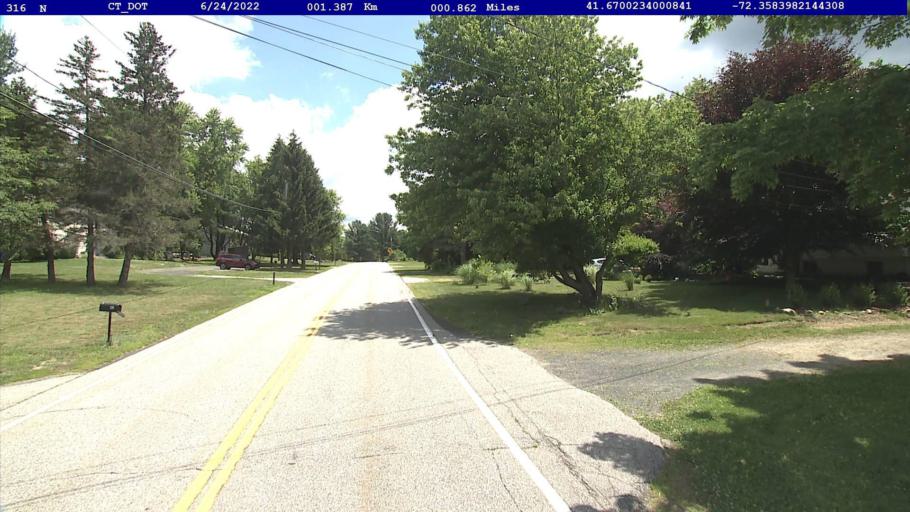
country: US
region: Connecticut
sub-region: Tolland County
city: Hebron
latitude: 41.6700
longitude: -72.3583
